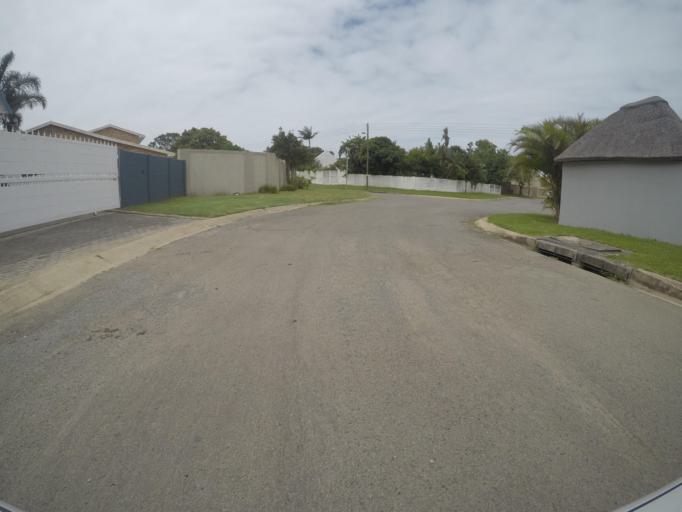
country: ZA
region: Eastern Cape
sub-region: Buffalo City Metropolitan Municipality
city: East London
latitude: -32.9796
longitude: 27.9497
